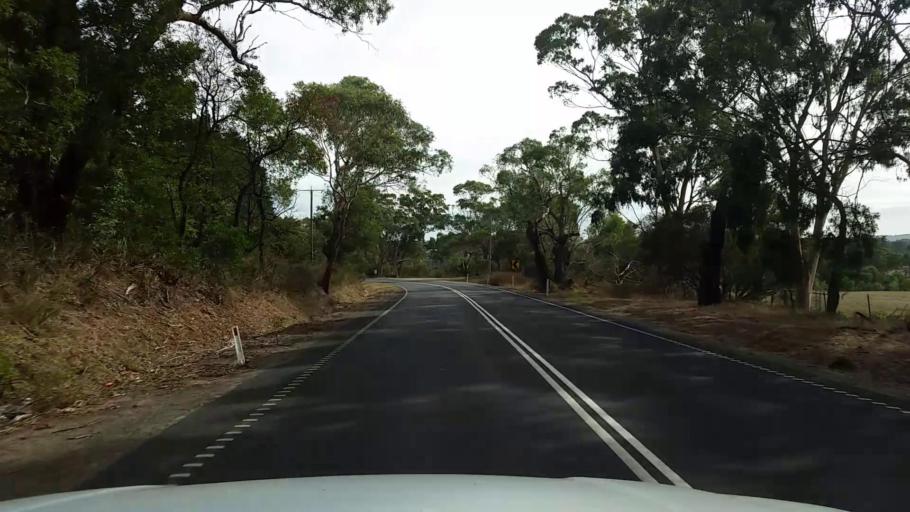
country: AU
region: Victoria
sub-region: Mornington Peninsula
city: Mount Martha
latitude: -38.2858
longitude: 145.0707
